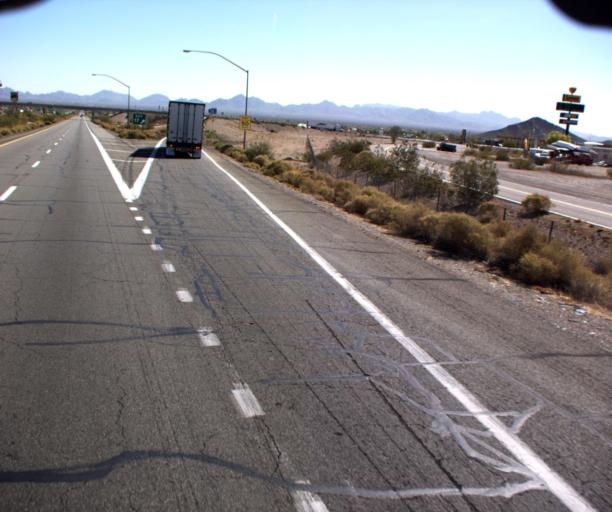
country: US
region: Arizona
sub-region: La Paz County
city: Quartzsite
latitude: 33.6591
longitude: -114.2444
